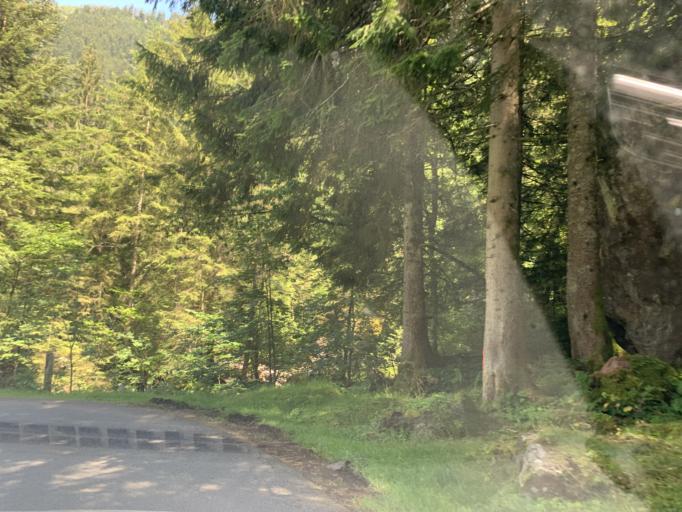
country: CH
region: Saint Gallen
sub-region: Wahlkreis Sarganserland
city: Quarten
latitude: 47.0867
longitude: 9.2035
